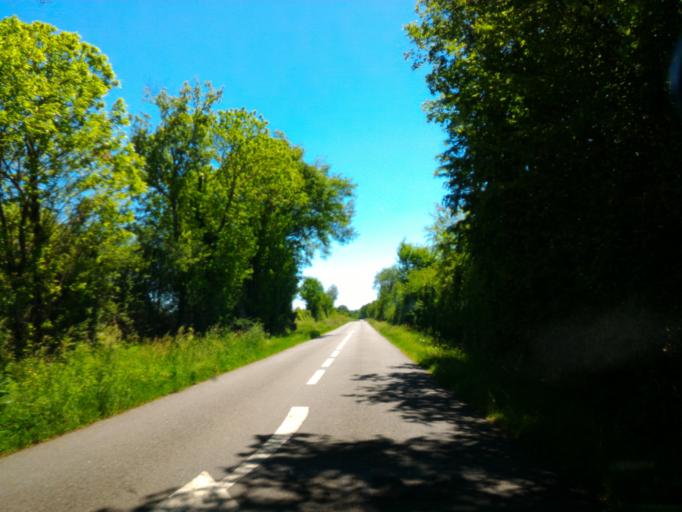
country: FR
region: Poitou-Charentes
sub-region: Departement de la Charente
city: Confolens
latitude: 46.0783
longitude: 0.7649
